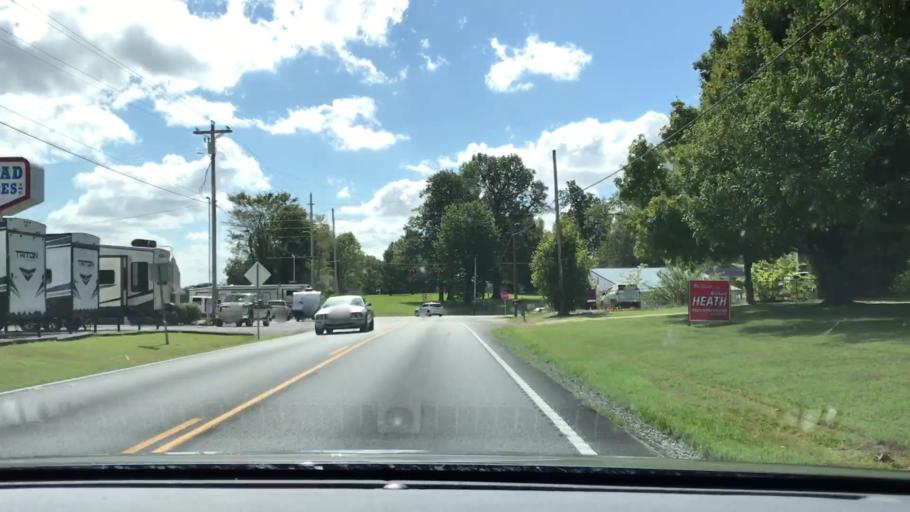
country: US
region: Kentucky
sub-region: Graves County
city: Mayfield
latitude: 36.7605
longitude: -88.5962
